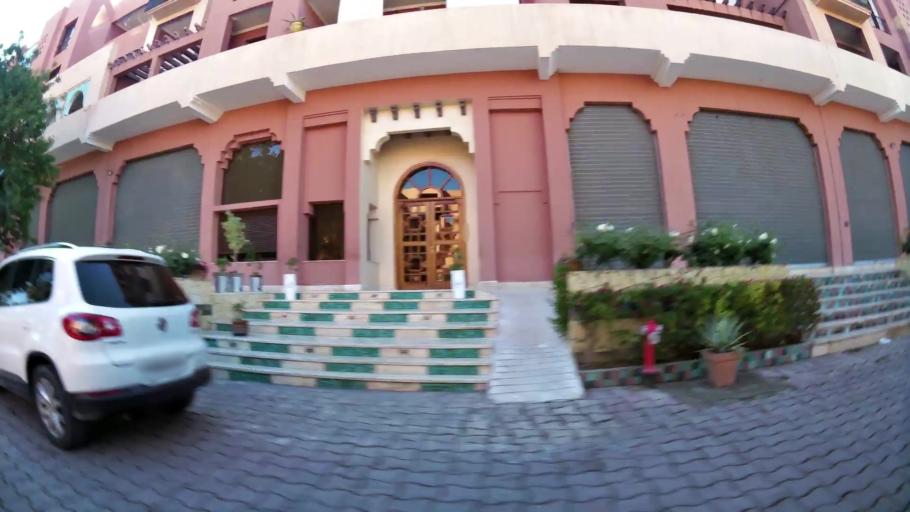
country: MA
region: Marrakech-Tensift-Al Haouz
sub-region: Marrakech
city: Marrakesh
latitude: 31.6475
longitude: -8.0174
